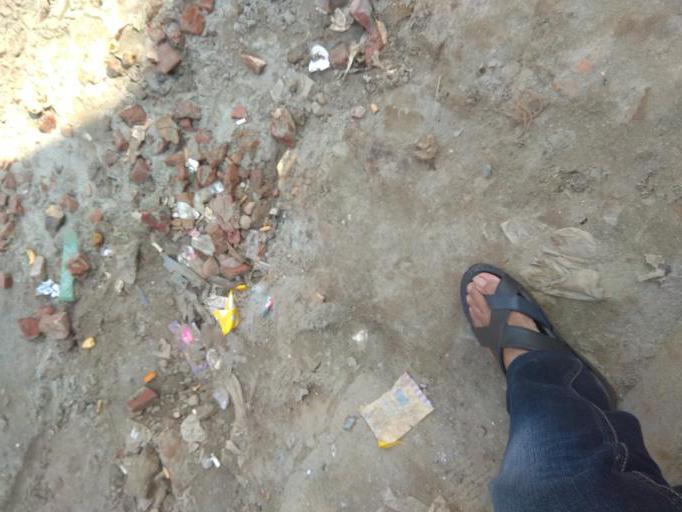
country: BD
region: Dhaka
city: Tungi
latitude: 23.8205
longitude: 90.3712
